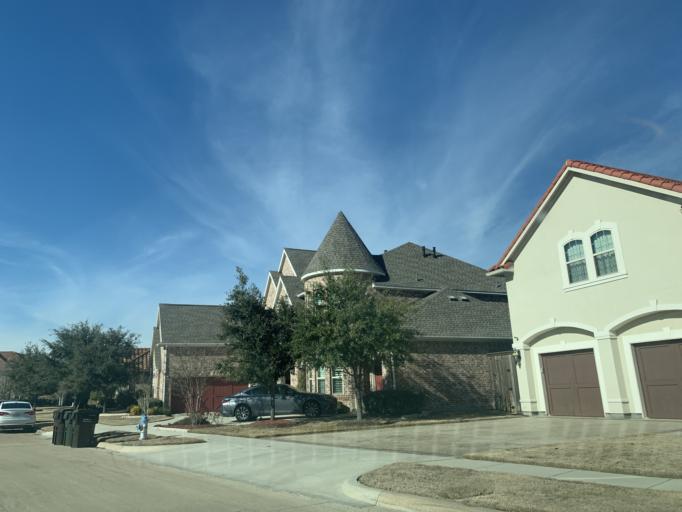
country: US
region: Texas
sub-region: Denton County
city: The Colony
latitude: 33.0570
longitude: -96.8140
